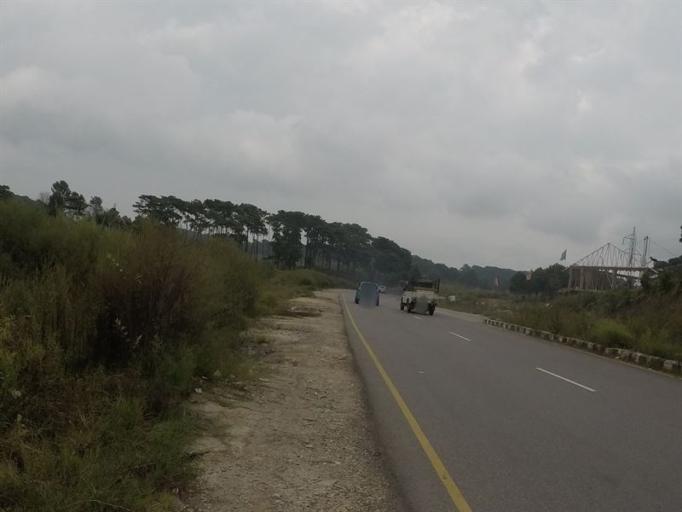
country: IN
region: Meghalaya
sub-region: East Khasi Hills
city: Shillong
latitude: 25.4954
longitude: 92.1723
